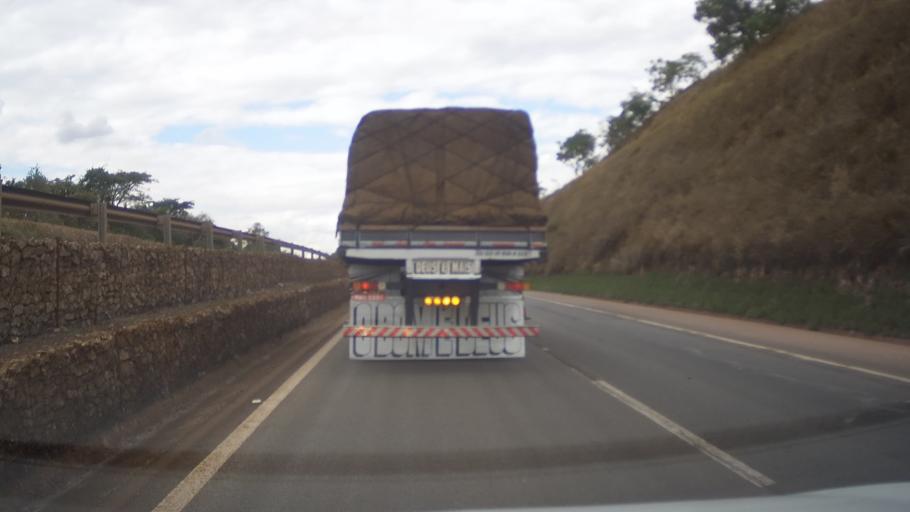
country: BR
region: Minas Gerais
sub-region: Itauna
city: Itauna
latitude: -20.3168
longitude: -44.4531
